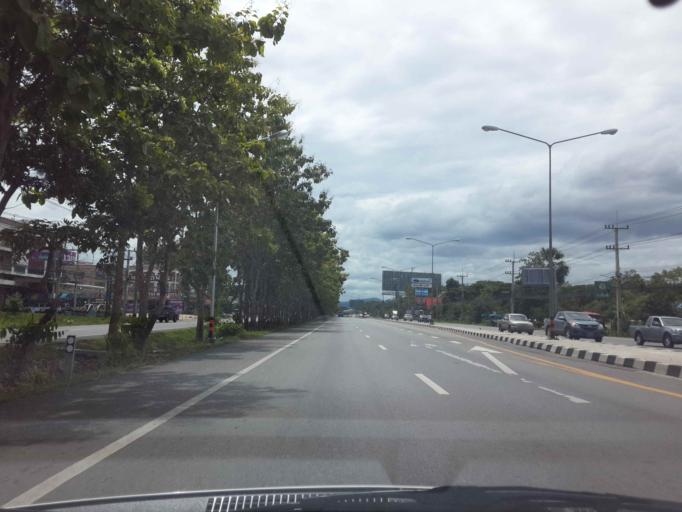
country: TH
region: Phetchaburi
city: Phetchaburi
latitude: 13.1231
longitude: 99.8871
